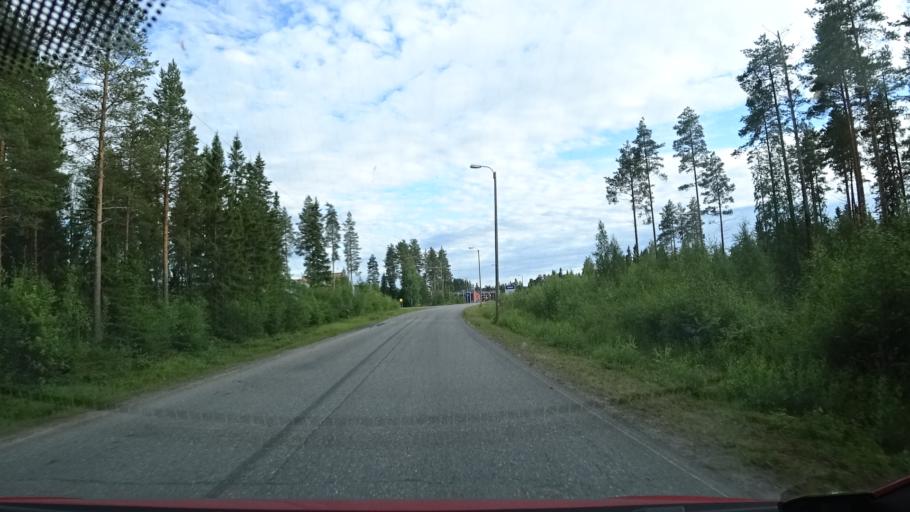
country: FI
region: Northern Ostrobothnia
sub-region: Oulu
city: Haukipudas
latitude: 65.1987
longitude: 25.4136
